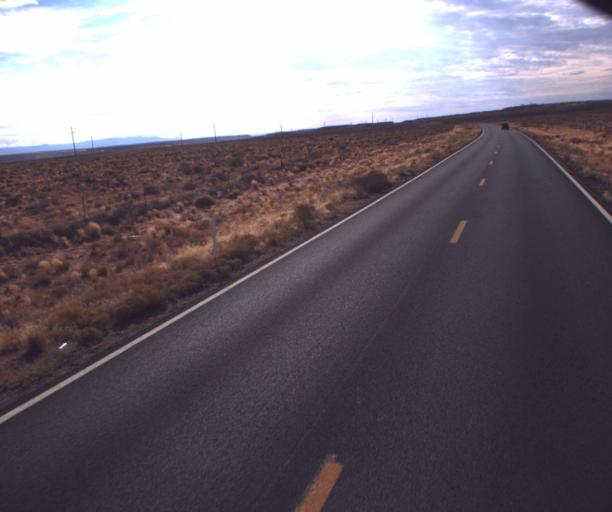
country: US
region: Arizona
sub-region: Apache County
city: Many Farms
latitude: 36.6170
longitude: -109.5803
